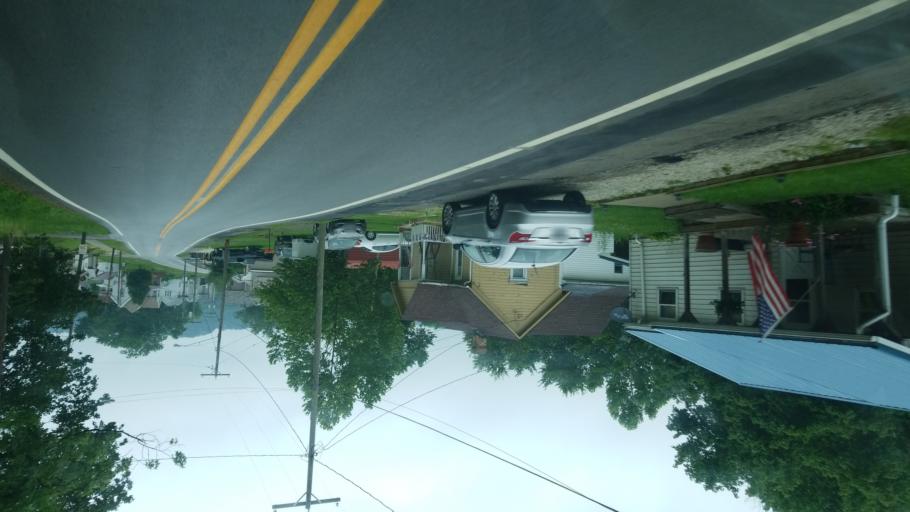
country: US
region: Ohio
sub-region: Columbiana County
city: Salineville
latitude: 40.5172
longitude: -80.8874
